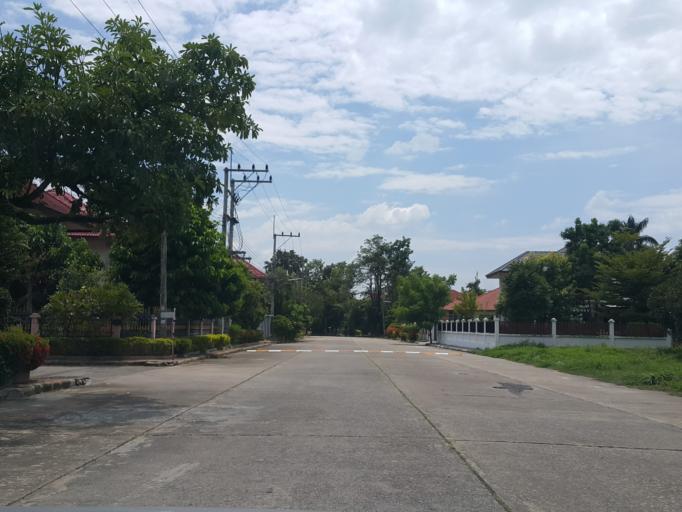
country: TH
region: Chiang Mai
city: Hang Dong
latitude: 18.7404
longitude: 98.9417
